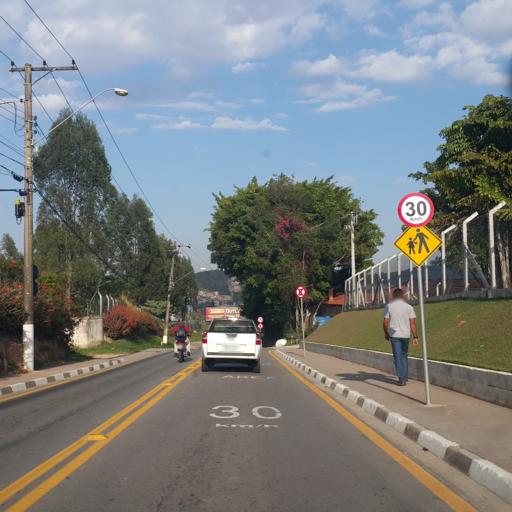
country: BR
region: Sao Paulo
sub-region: Louveira
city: Louveira
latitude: -23.0834
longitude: -46.9719
